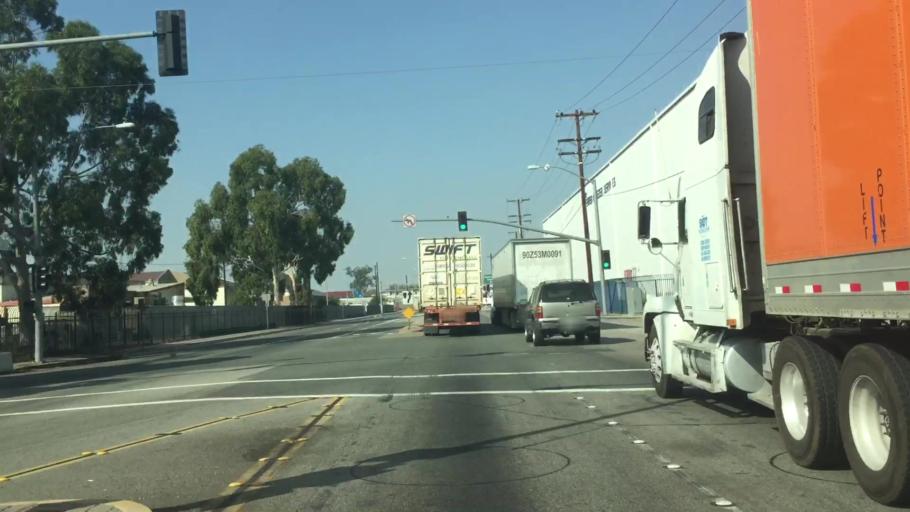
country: US
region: California
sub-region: Los Angeles County
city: Commerce
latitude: 33.9972
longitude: -118.1719
